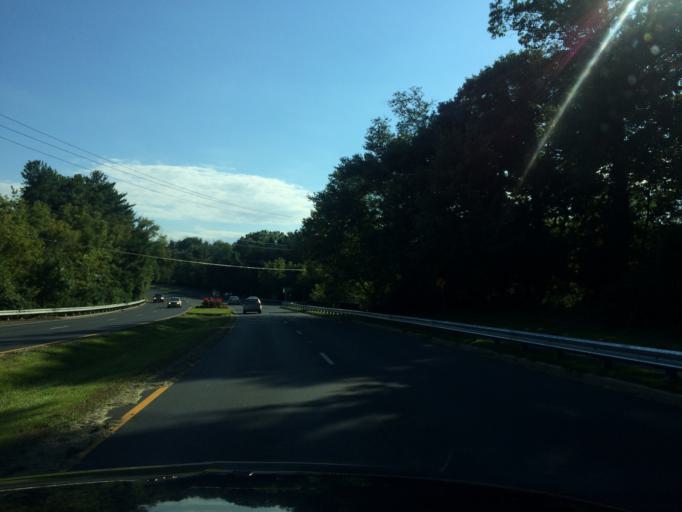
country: US
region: Maryland
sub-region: Montgomery County
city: Rockville
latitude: 39.0877
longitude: -77.1343
